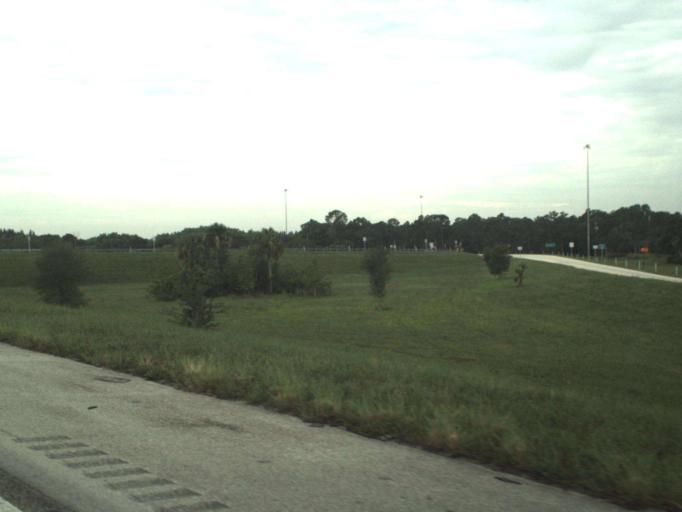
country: US
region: Florida
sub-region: Martin County
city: Palm City
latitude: 27.1115
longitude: -80.2624
